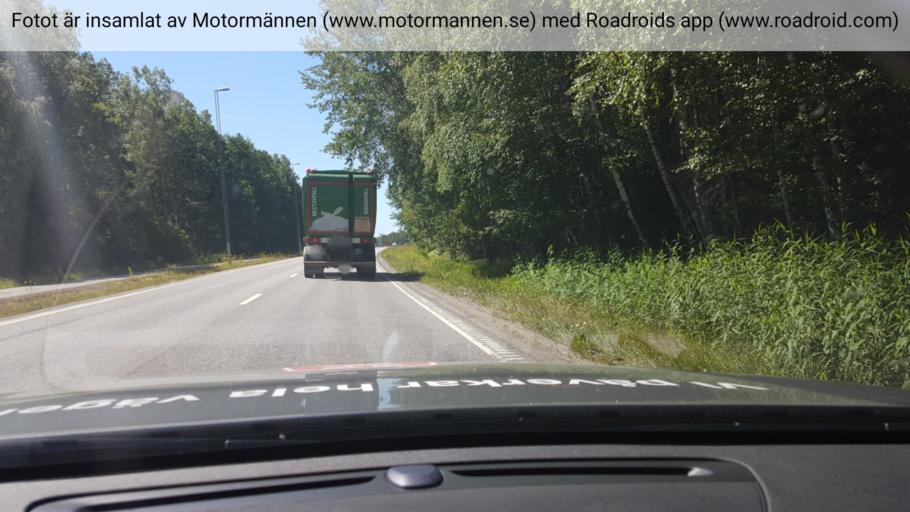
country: SE
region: Stockholm
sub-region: Haninge Kommun
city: Haninge
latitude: 59.1950
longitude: 18.1837
